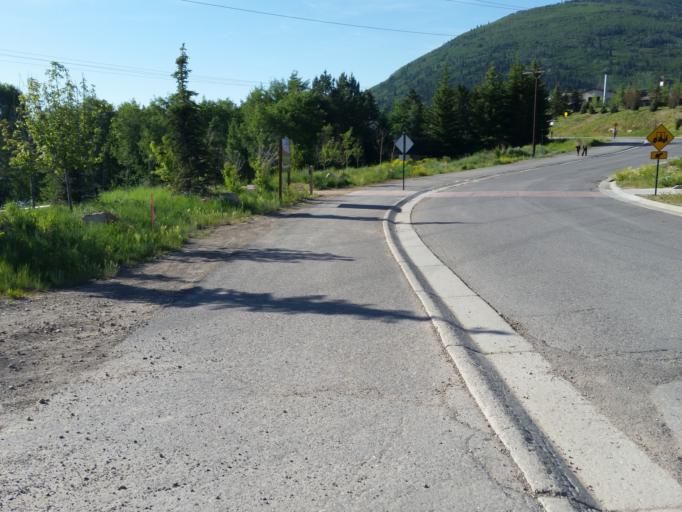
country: US
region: Utah
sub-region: Summit County
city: Snyderville
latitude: 40.6893
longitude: -111.5498
